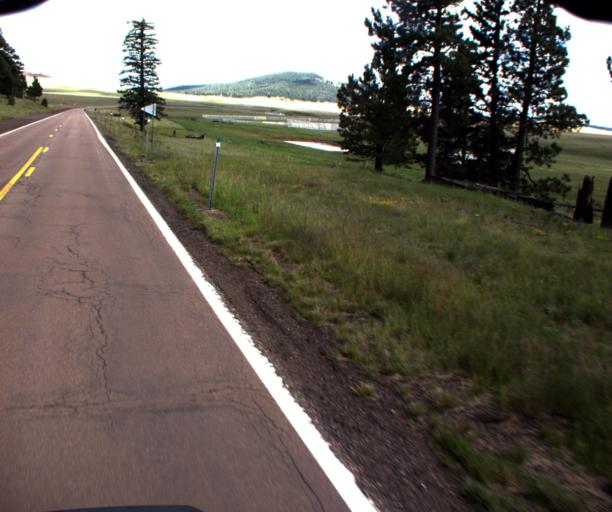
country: US
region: Arizona
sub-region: Apache County
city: Eagar
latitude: 34.0544
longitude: -109.5556
